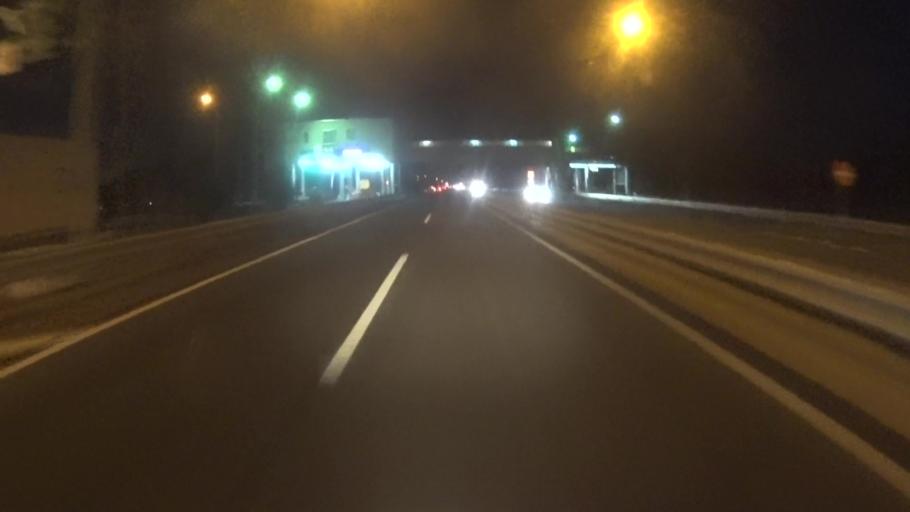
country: JP
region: Kyoto
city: Kameoka
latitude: 35.0160
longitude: 135.5554
